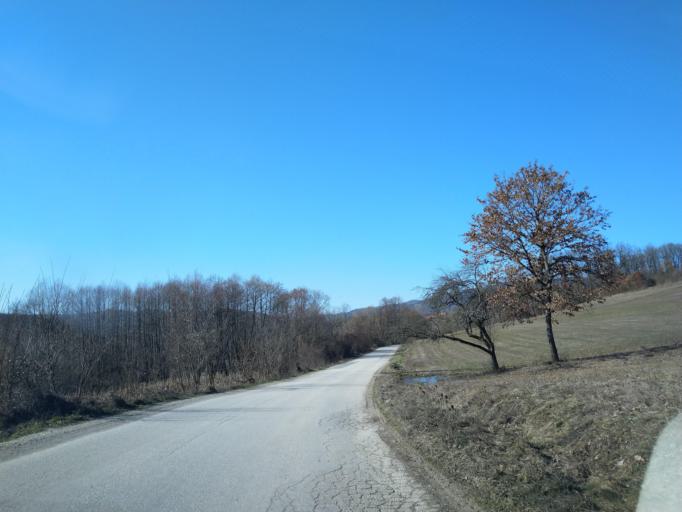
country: RS
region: Central Serbia
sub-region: Zlatiborski Okrug
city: Kosjeric
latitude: 43.9321
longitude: 19.8896
